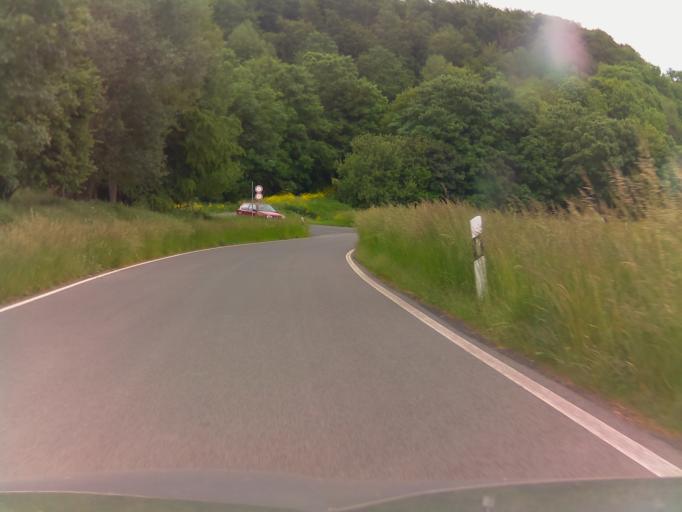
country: DE
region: Bavaria
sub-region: Regierungsbezirk Unterfranken
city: Oberelsbach
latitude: 50.4421
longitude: 10.0628
